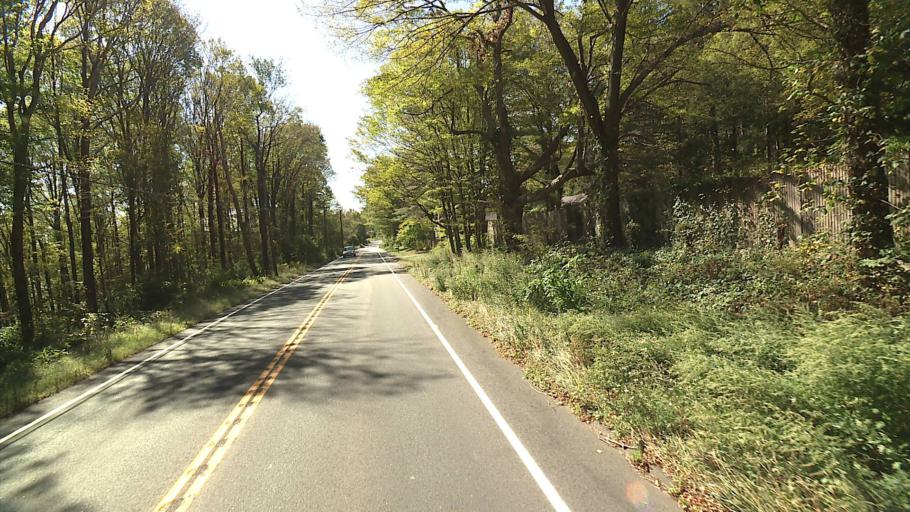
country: US
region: Connecticut
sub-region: New Haven County
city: Woodbridge
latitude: 41.4170
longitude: -72.9731
